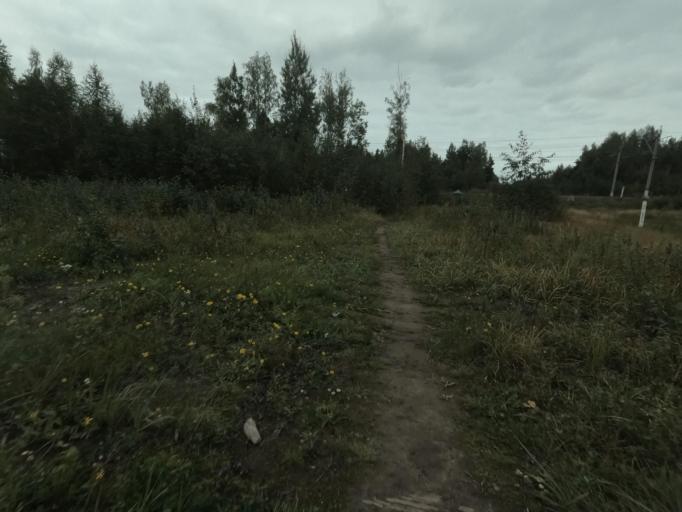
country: RU
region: St.-Petersburg
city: Sapernyy
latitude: 59.7649
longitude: 30.7255
